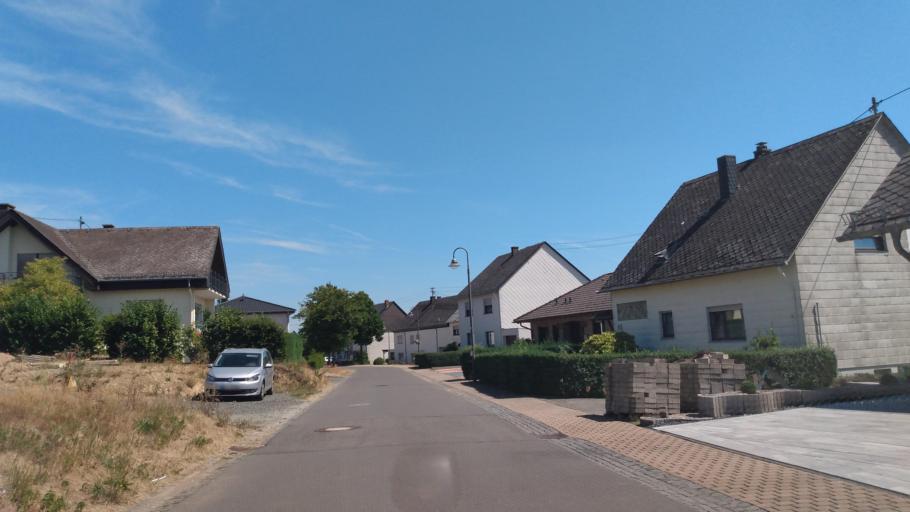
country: DE
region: Rheinland-Pfalz
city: Merschbach
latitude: 49.8085
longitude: 7.0283
